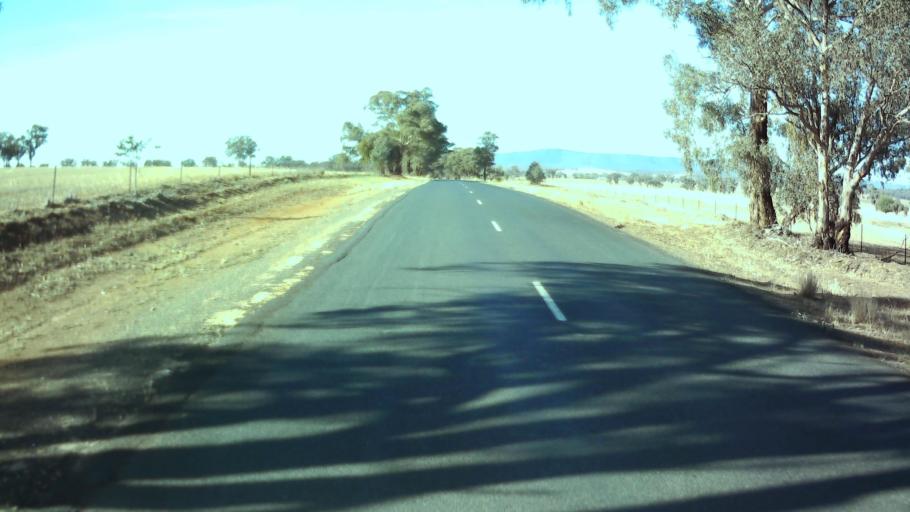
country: AU
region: New South Wales
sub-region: Weddin
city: Grenfell
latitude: -33.9199
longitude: 148.1408
